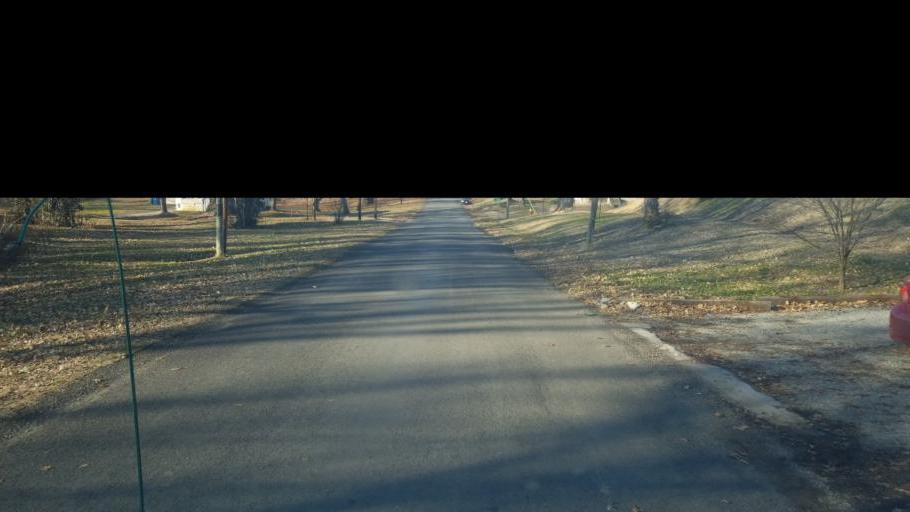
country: US
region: Illinois
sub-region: Wabash County
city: Mount Carmel
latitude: 38.4137
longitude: -87.7557
